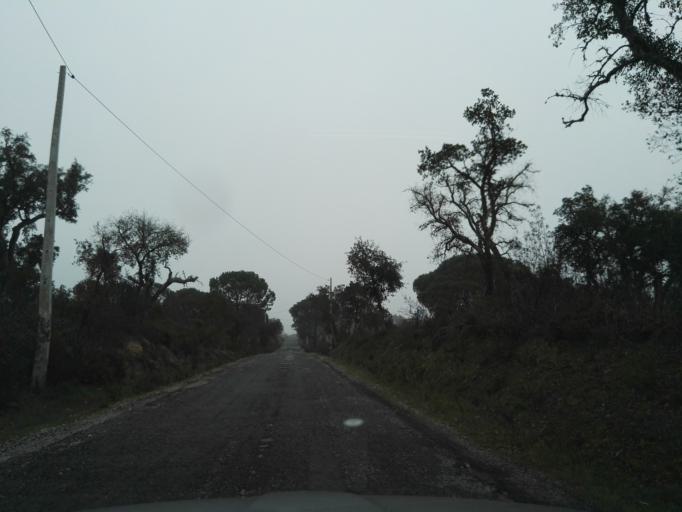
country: PT
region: Evora
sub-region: Vendas Novas
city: Vendas Novas
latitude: 38.7922
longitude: -8.3494
